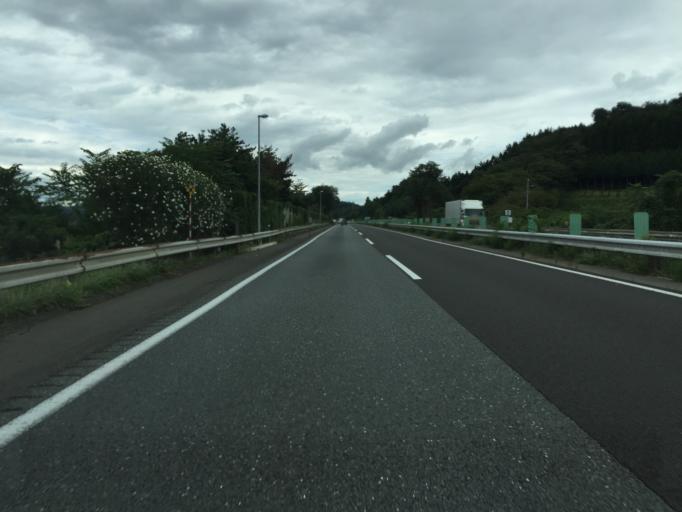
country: JP
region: Miyagi
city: Okawara
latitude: 38.1087
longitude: 140.6938
